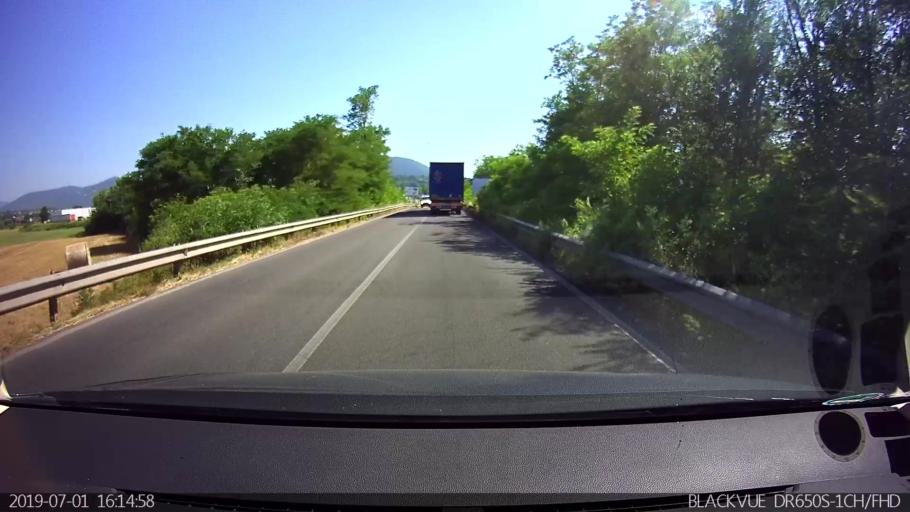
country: IT
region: Latium
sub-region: Provincia di Frosinone
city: Ceccano
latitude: 41.5974
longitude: 13.2925
